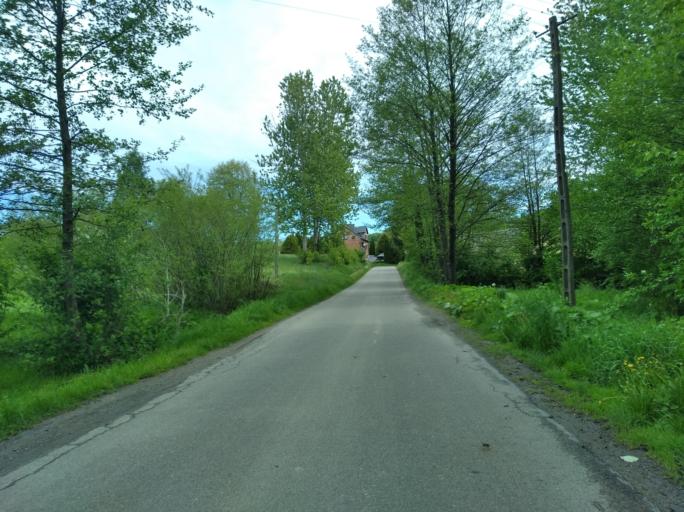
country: PL
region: Subcarpathian Voivodeship
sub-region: Powiat strzyzowski
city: Strzyzow
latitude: 49.9276
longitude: 21.7685
